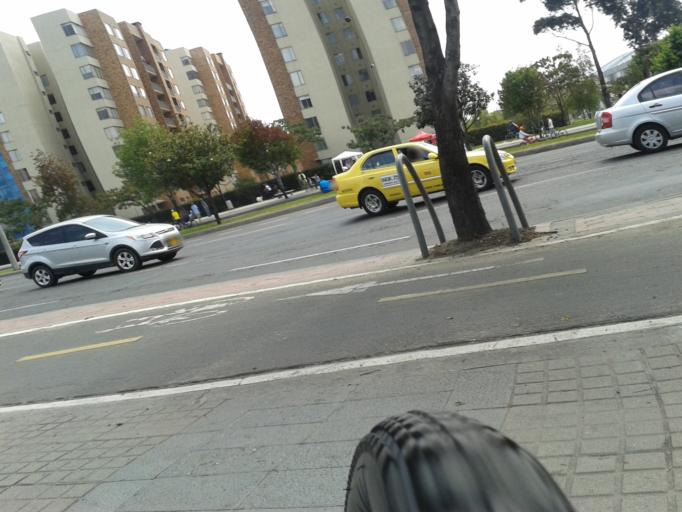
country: CO
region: Bogota D.C.
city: Barrio San Luis
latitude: 4.7266
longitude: -74.0710
